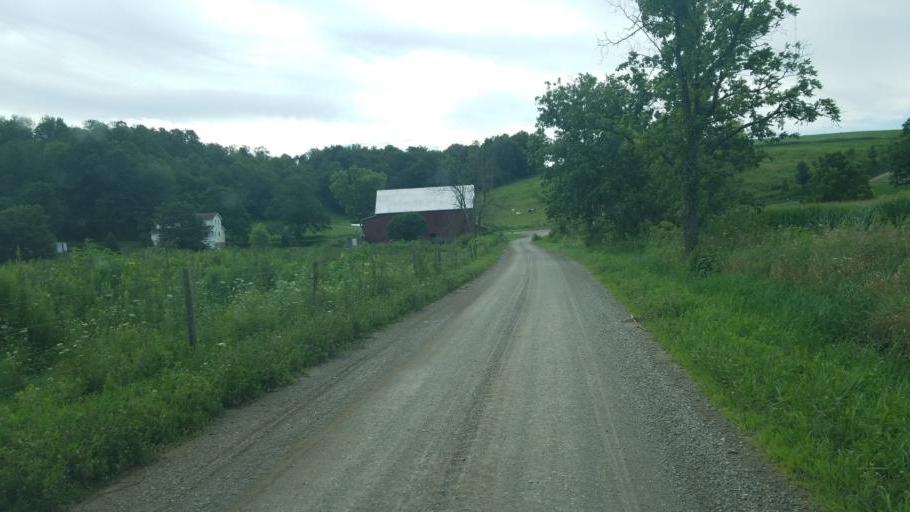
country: US
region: Ohio
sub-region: Holmes County
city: Millersburg
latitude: 40.4909
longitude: -81.8478
